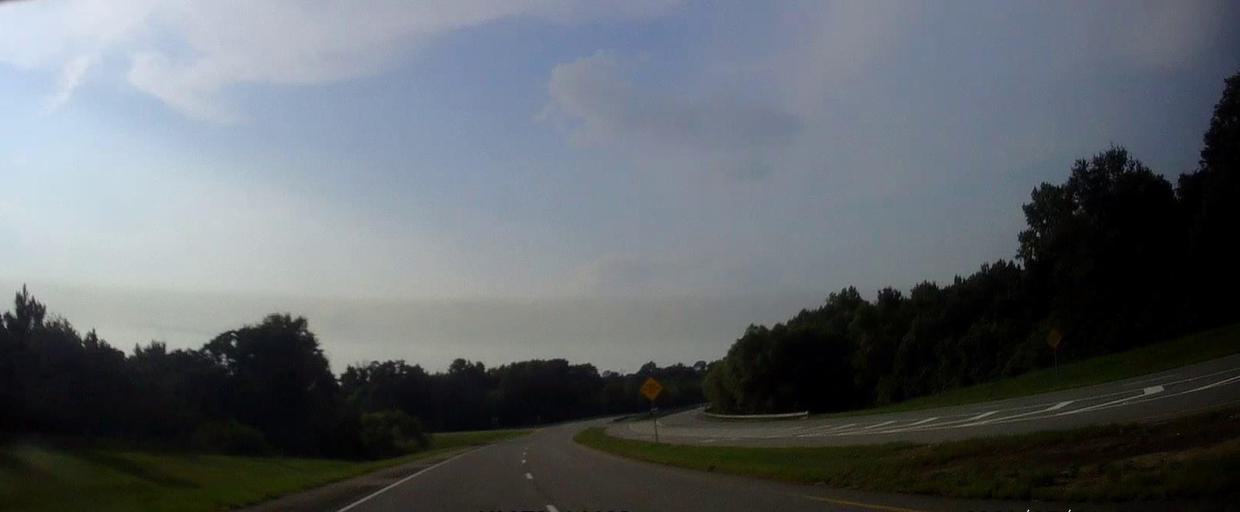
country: US
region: Georgia
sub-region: Laurens County
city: Dublin
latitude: 32.5442
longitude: -82.9774
